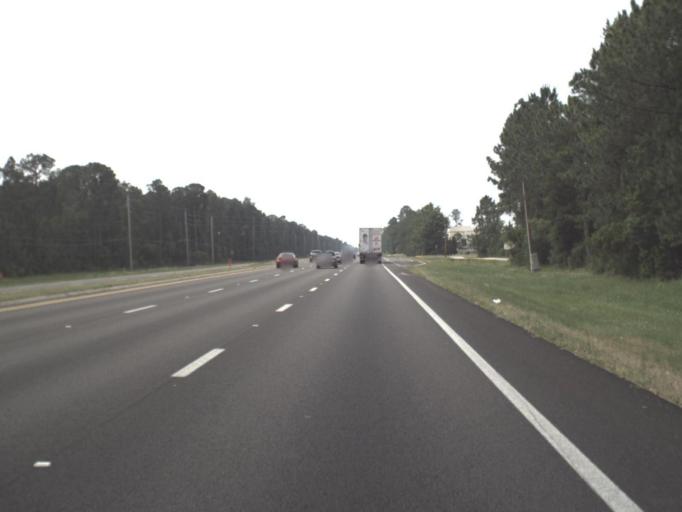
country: US
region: Florida
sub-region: Saint Johns County
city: Fruit Cove
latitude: 30.0943
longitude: -81.7062
